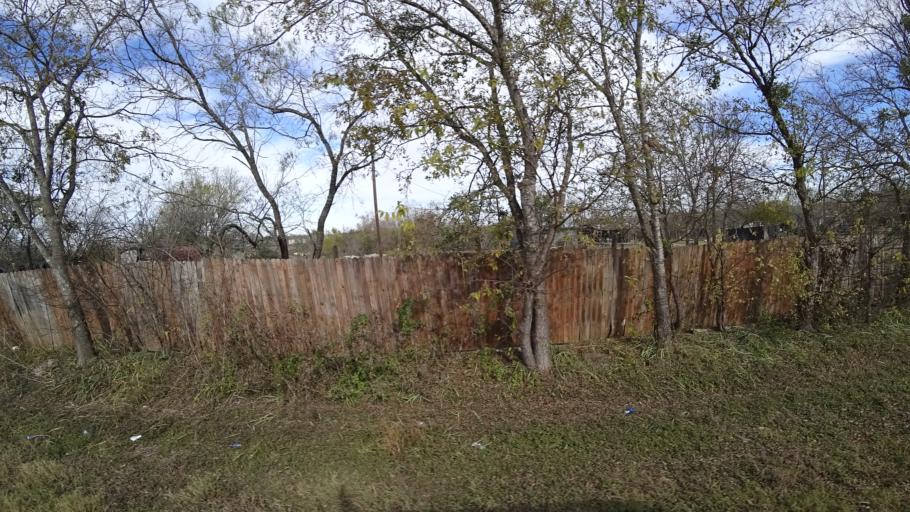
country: US
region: Texas
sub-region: Travis County
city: Onion Creek
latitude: 30.1150
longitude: -97.7217
